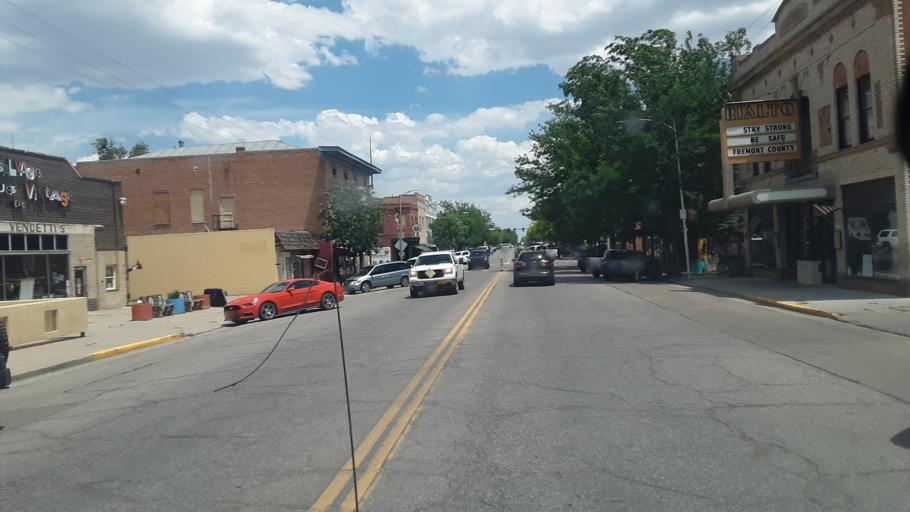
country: US
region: Colorado
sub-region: Fremont County
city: Florence
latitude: 38.3904
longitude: -105.1203
